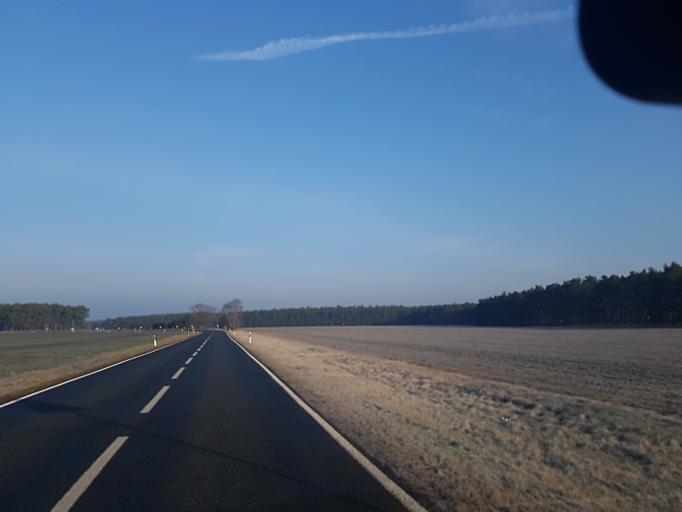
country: DE
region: Brandenburg
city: Golzow
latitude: 52.2516
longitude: 12.6909
